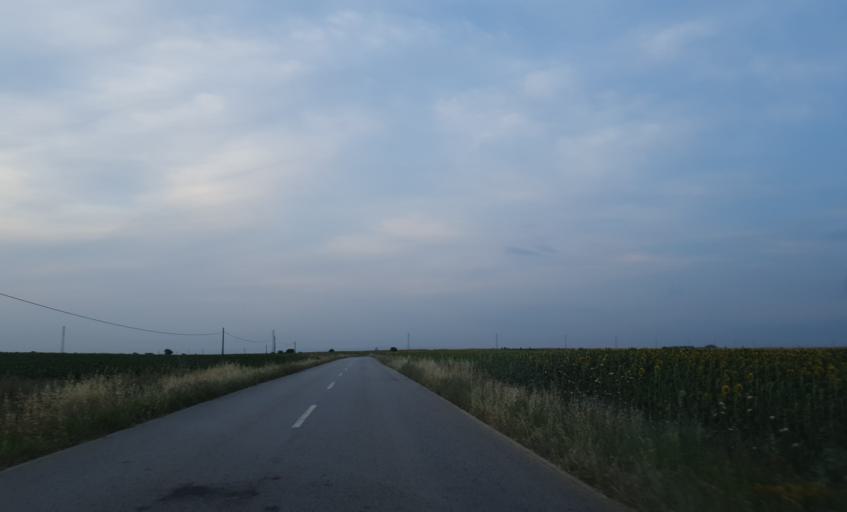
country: TR
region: Kirklareli
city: Buyukkaristiran
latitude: 41.3260
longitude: 27.6065
